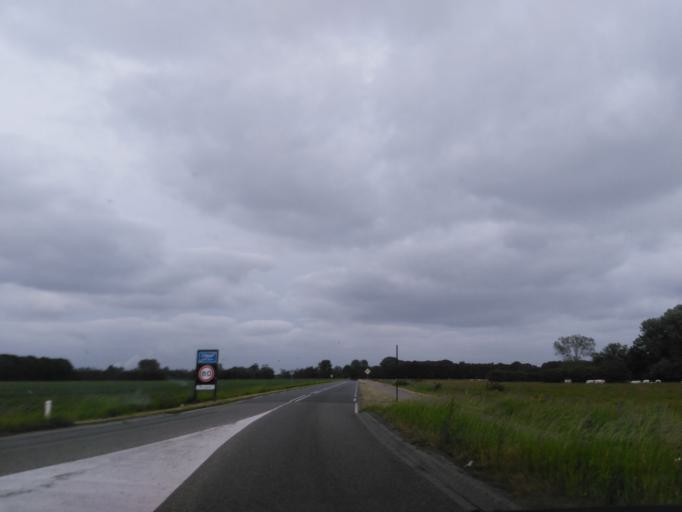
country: NL
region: Zeeland
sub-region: Gemeente Hulst
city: Hulst
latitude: 51.2740
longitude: 4.0954
